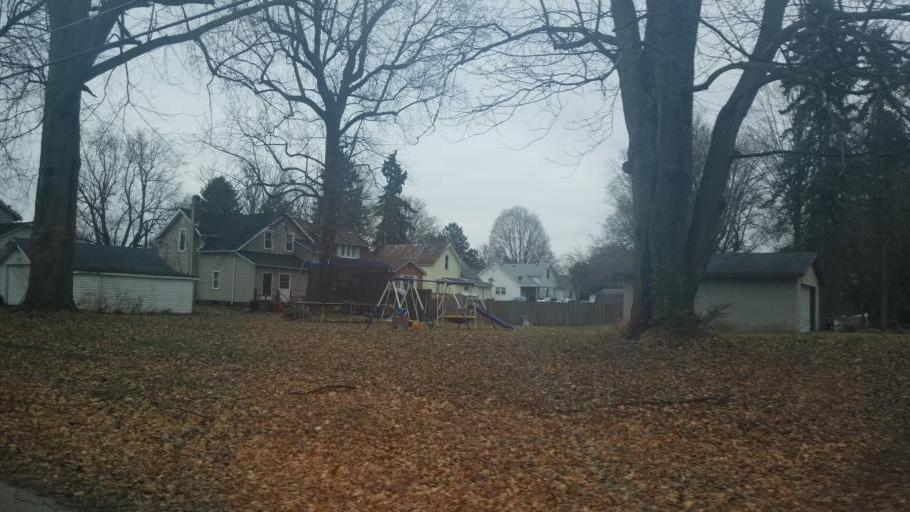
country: US
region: Ohio
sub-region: Crawford County
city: Galion
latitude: 40.7397
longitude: -82.7858
